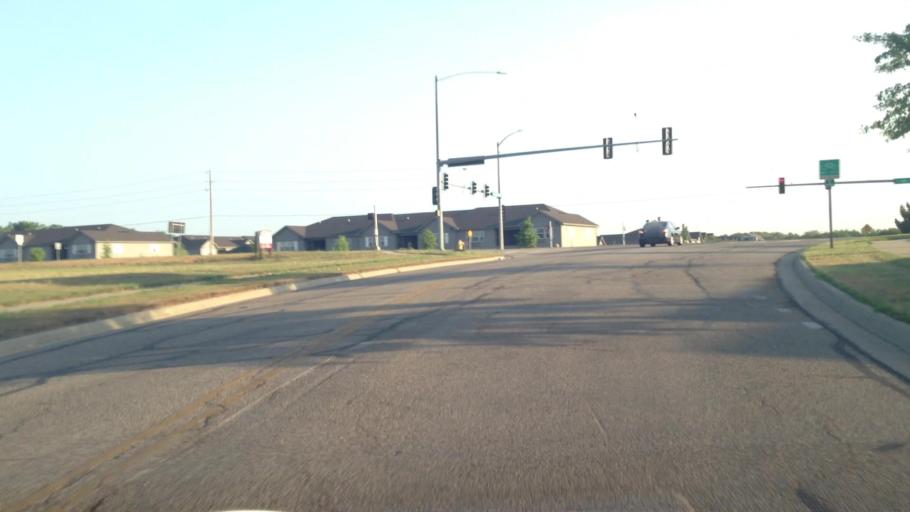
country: US
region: Kansas
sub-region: Douglas County
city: Lawrence
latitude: 38.9708
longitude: -95.3111
